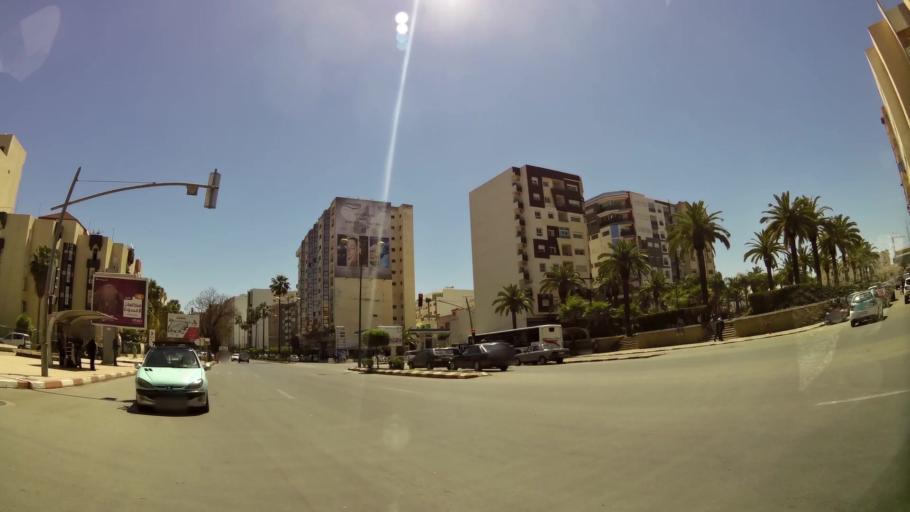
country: MA
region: Meknes-Tafilalet
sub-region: Meknes
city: Meknes
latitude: 33.8985
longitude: -5.5325
